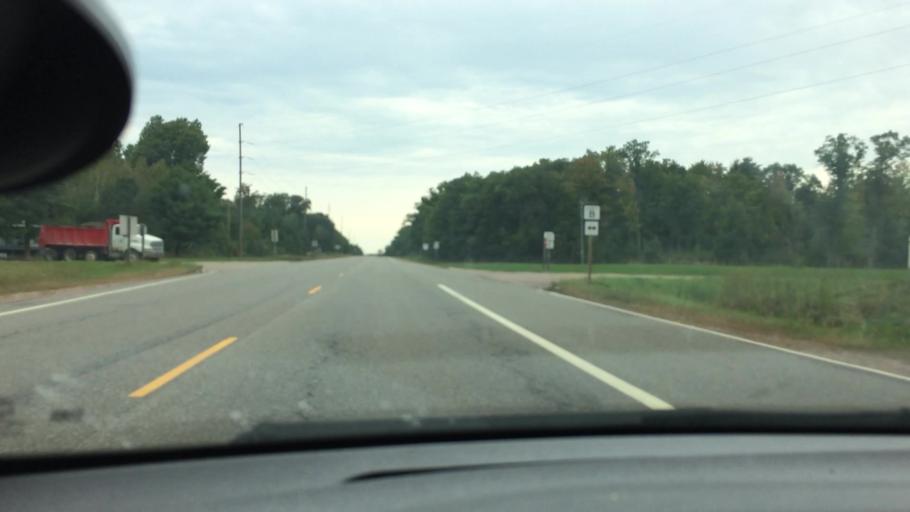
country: US
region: Wisconsin
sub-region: Clark County
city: Neillsville
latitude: 44.5725
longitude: -90.7299
